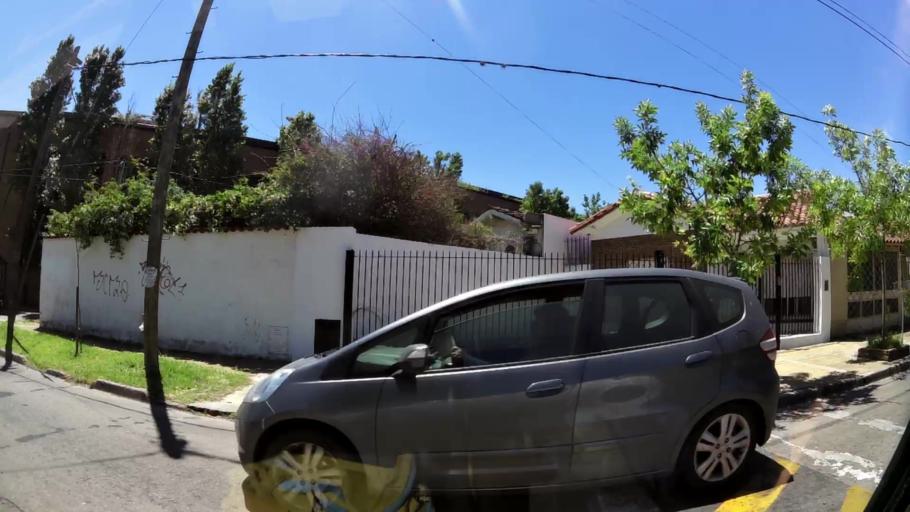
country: AR
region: Buenos Aires
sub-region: Partido de San Isidro
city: San Isidro
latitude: -34.4903
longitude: -58.5195
